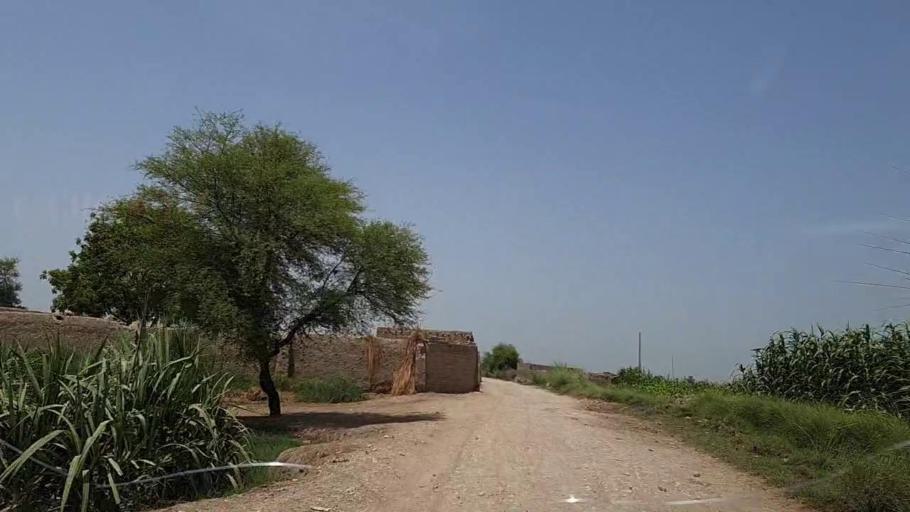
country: PK
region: Sindh
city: Tharu Shah
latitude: 26.9247
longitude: 68.0559
